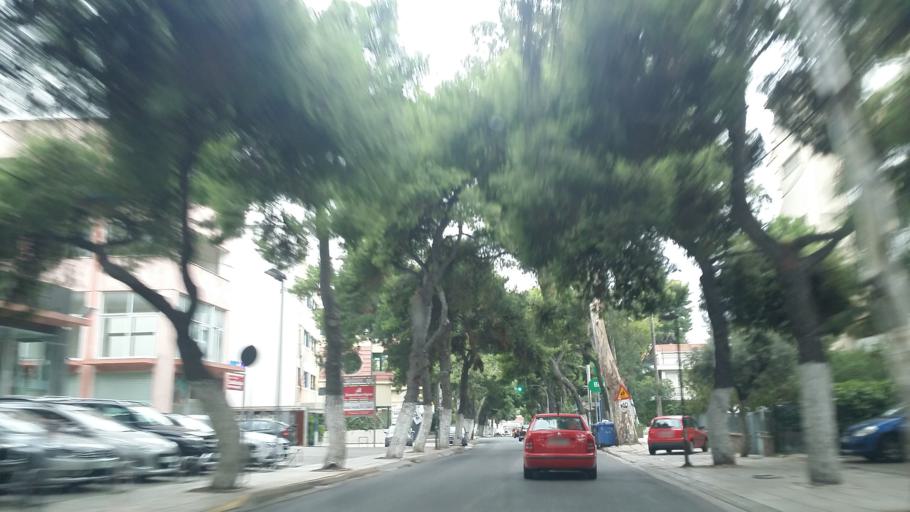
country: GR
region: Attica
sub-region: Nomarchia Athinas
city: Metamorfosi
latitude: 38.0644
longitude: 23.7587
